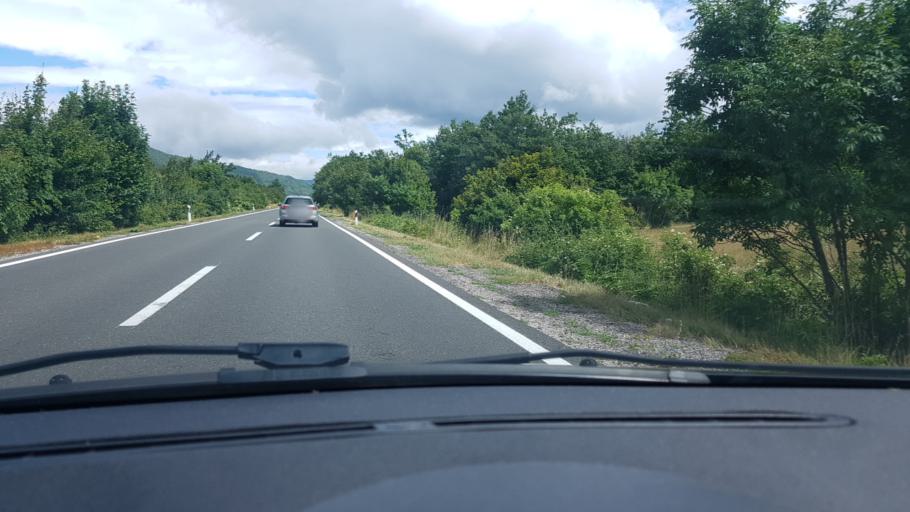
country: HR
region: Zadarska
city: Gracac
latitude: 44.4570
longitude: 15.8202
